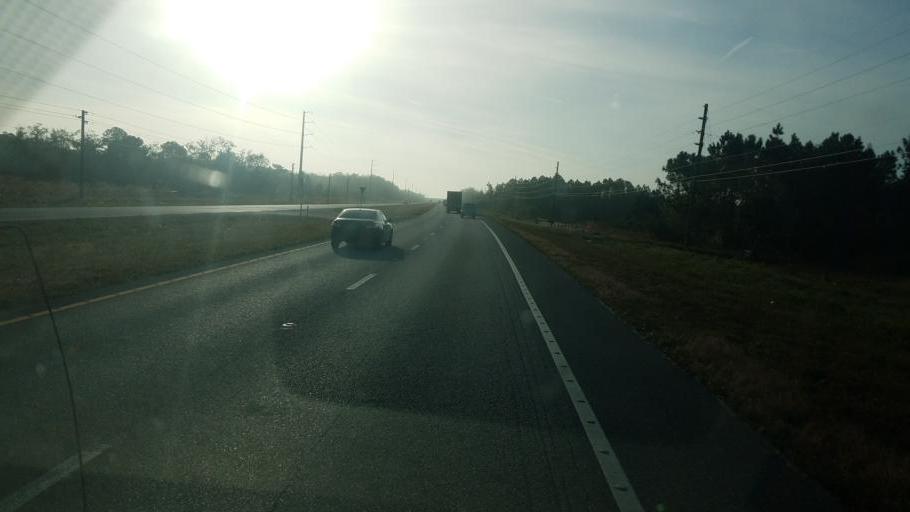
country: US
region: Florida
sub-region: Osceola County
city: Saint Cloud
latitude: 28.1690
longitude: -81.1275
